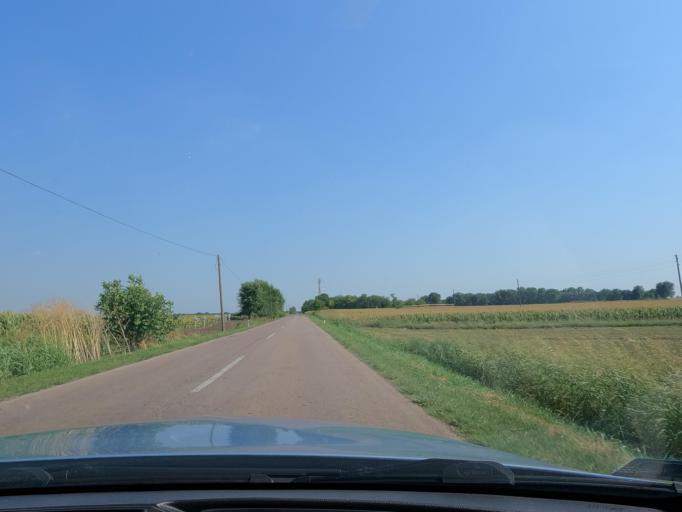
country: RS
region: Autonomna Pokrajina Vojvodina
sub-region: Severnobacki Okrug
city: Mali Igos
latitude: 45.7720
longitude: 19.7328
